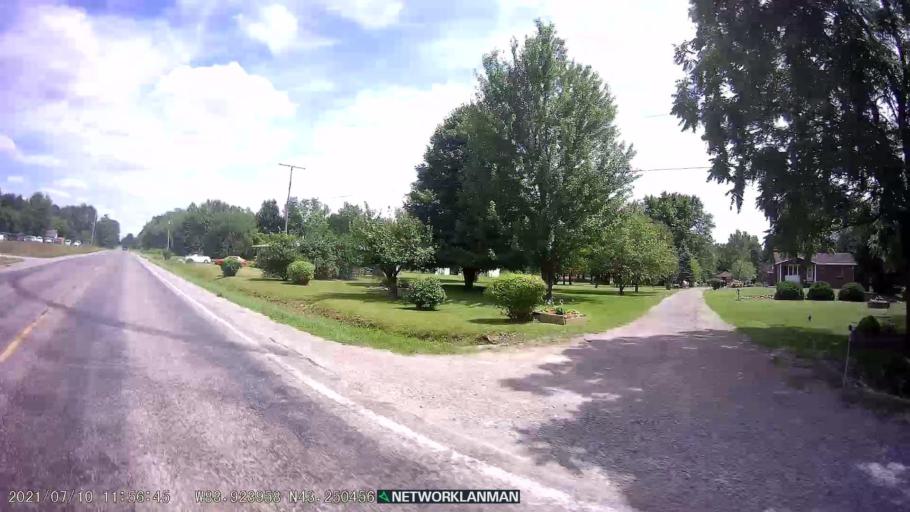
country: US
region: Michigan
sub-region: Saginaw County
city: Burt
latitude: 43.2502
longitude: -83.9236
